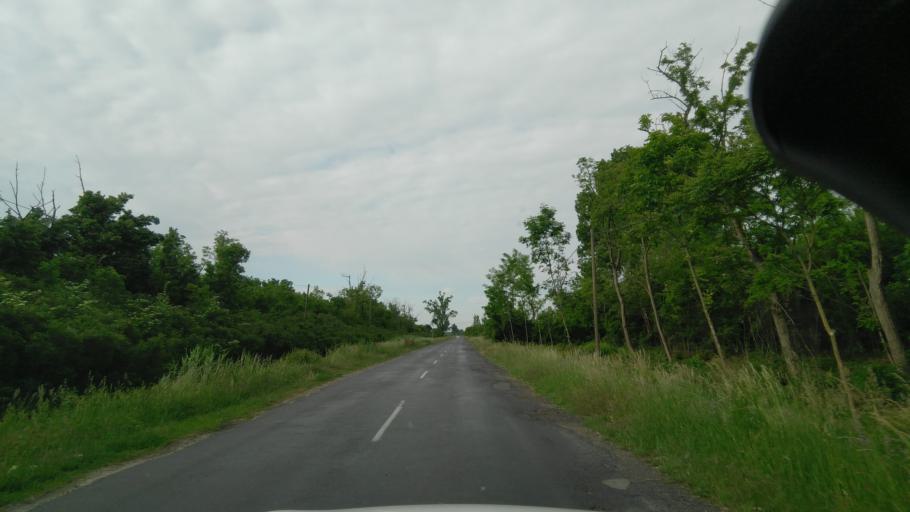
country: HU
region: Bekes
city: Elek
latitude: 46.5871
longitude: 21.2252
